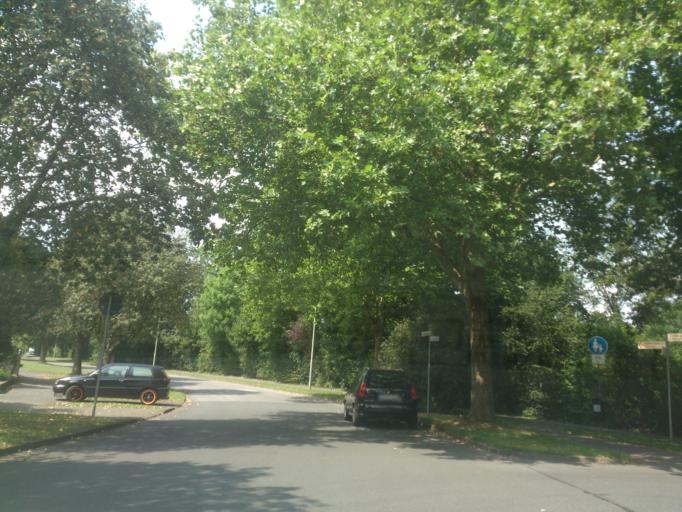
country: DE
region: North Rhine-Westphalia
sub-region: Regierungsbezirk Detmold
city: Paderborn
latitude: 51.7147
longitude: 8.7781
